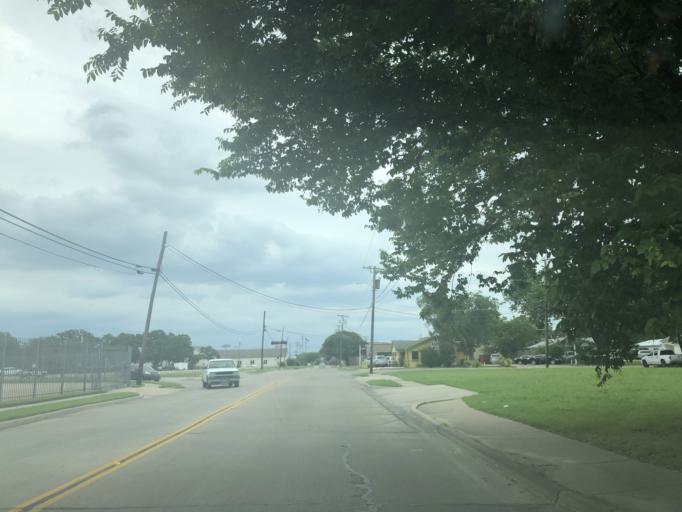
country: US
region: Texas
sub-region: Dallas County
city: Irving
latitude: 32.8085
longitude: -96.9307
